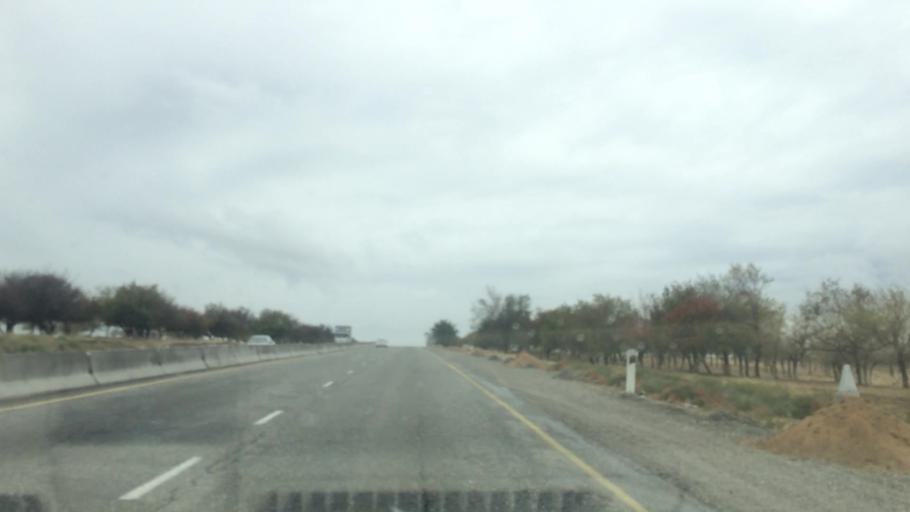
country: UZ
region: Samarqand
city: Bulung'ur
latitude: 39.8605
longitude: 67.4700
